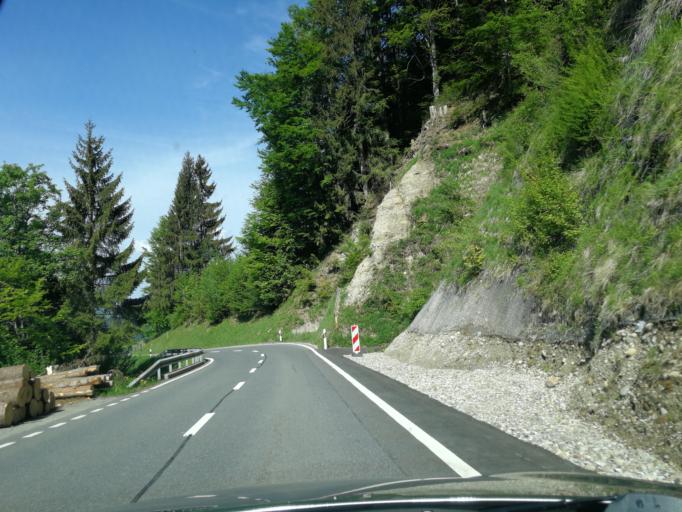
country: CH
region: Bern
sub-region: Emmental District
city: Eggiwil
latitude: 46.8247
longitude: 7.7904
